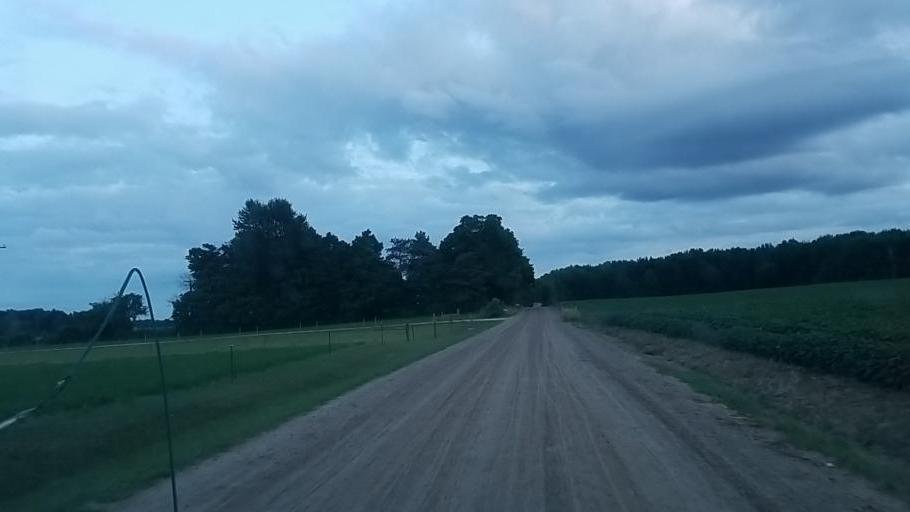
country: US
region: Michigan
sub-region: Newaygo County
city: Fremont
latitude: 43.4795
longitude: -86.0594
